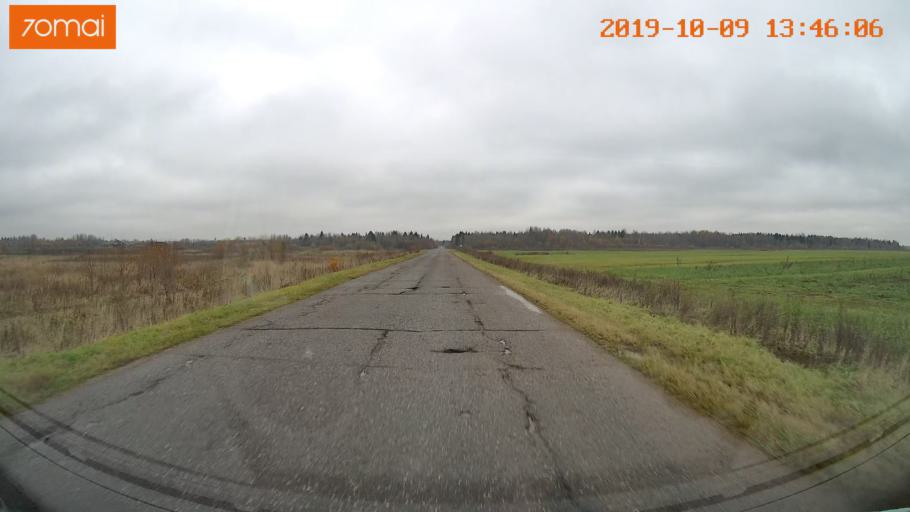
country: RU
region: Kostroma
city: Buy
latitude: 58.3805
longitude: 41.2153
